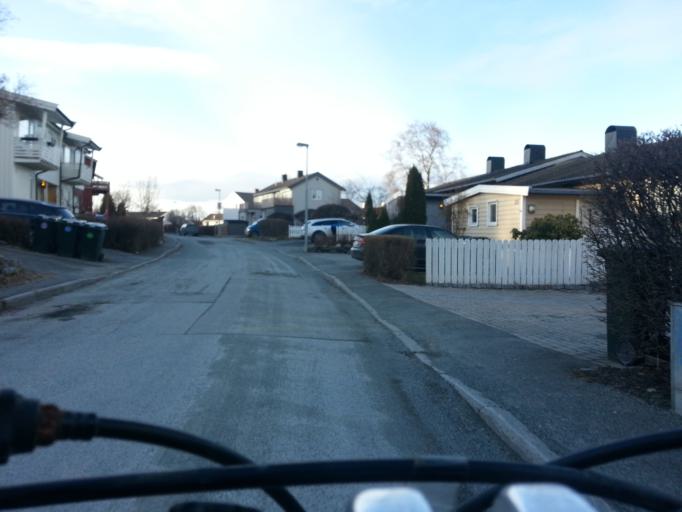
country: NO
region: Sor-Trondelag
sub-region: Trondheim
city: Trondheim
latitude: 63.4462
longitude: 10.4626
